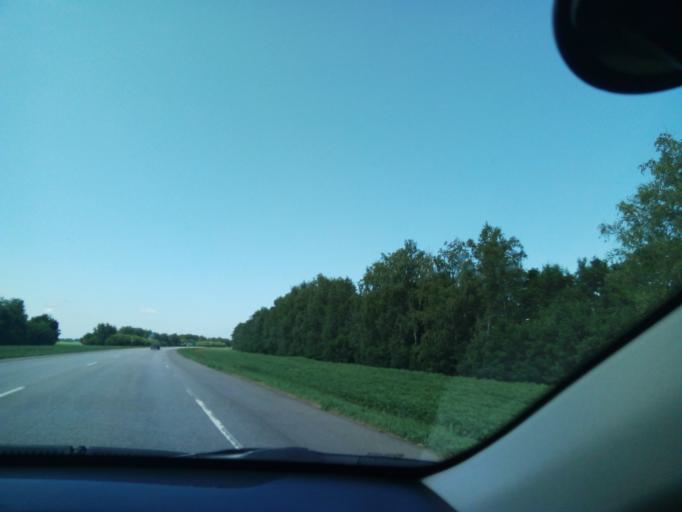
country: RU
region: Lipetsk
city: Gryazi
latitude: 52.5686
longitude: 40.1452
